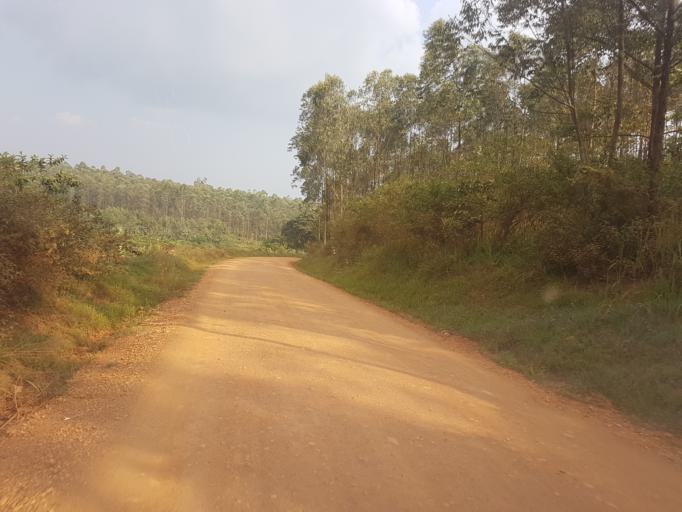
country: UG
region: Western Region
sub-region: Rukungiri District
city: Rukungiri
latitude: -0.6625
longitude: 29.8643
